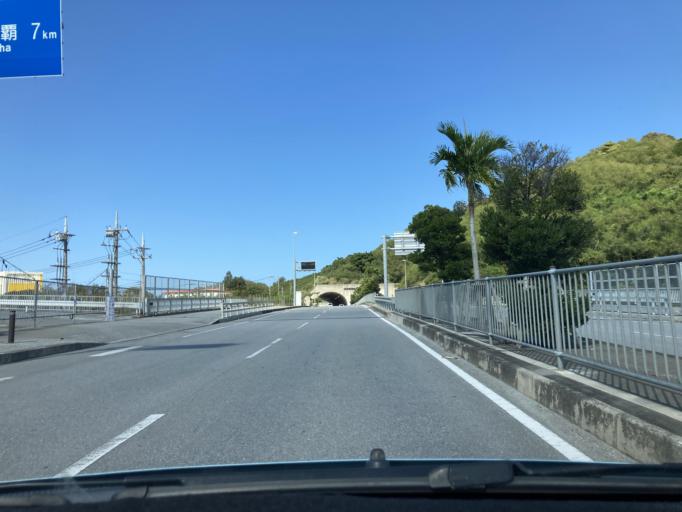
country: JP
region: Okinawa
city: Tomigusuku
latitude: 26.1852
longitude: 127.7214
